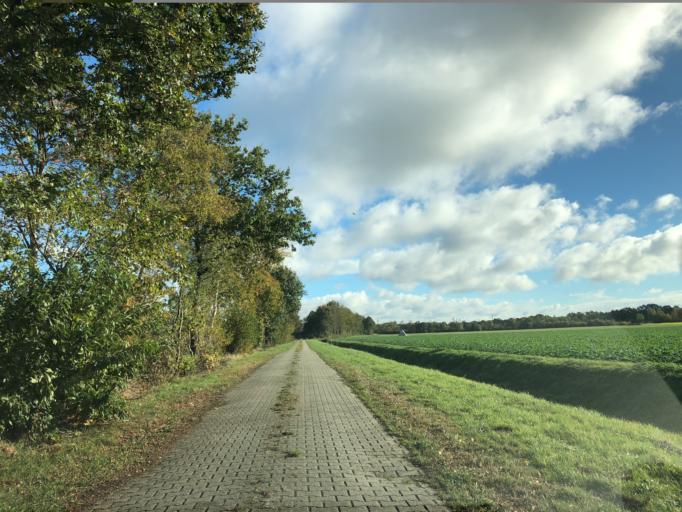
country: DE
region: Lower Saxony
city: Lehe
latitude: 53.0358
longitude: 7.3637
